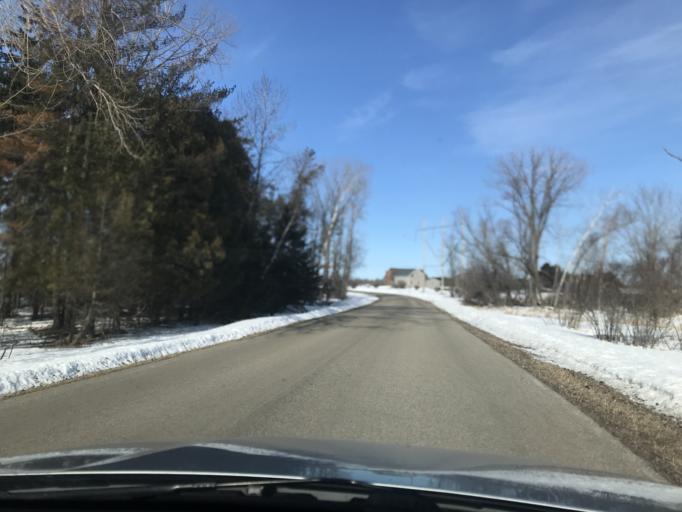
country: US
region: Wisconsin
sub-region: Oconto County
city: Oconto Falls
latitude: 44.9374
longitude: -88.1858
